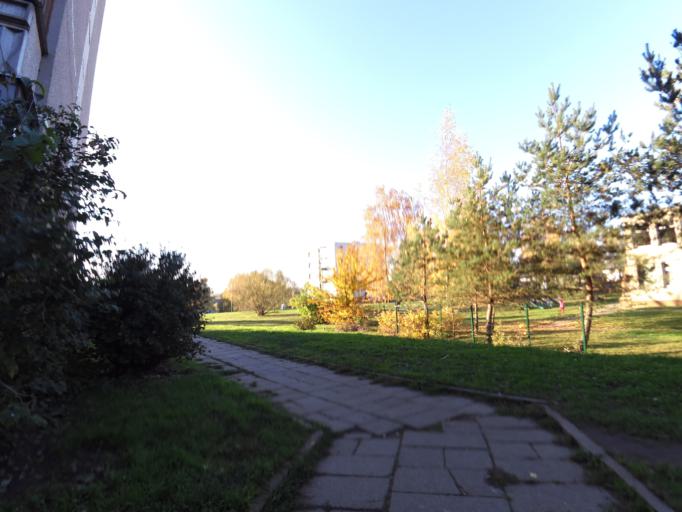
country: LT
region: Vilnius County
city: Justiniskes
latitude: 54.7212
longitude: 25.2120
